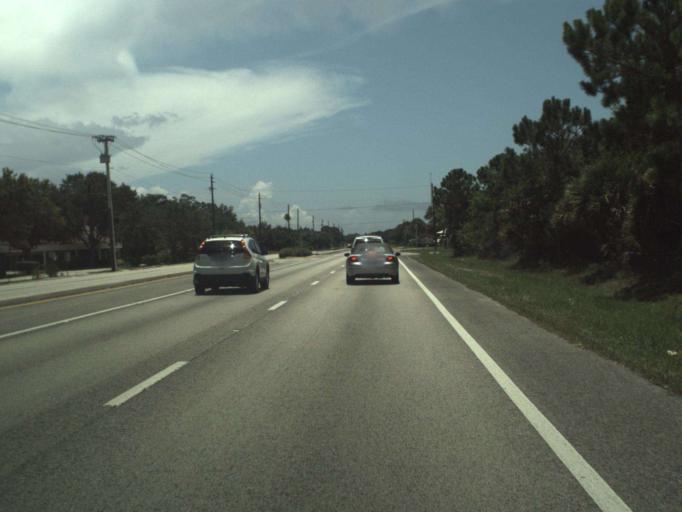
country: US
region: Florida
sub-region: Indian River County
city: Wabasso Beach
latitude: 27.7657
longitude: -80.4432
